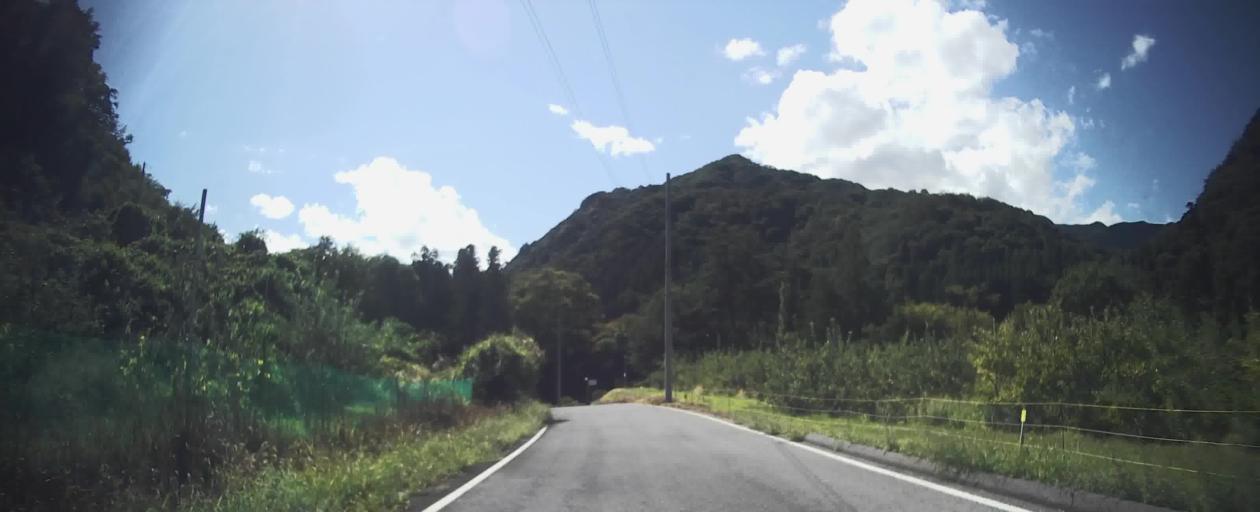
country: JP
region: Gunma
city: Nakanojomachi
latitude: 36.5686
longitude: 138.7329
